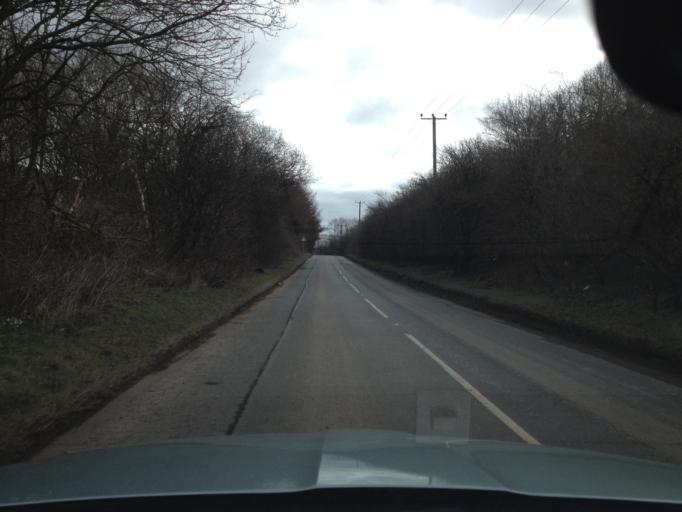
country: GB
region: Scotland
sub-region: West Lothian
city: Mid Calder
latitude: 55.9120
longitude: -3.4772
